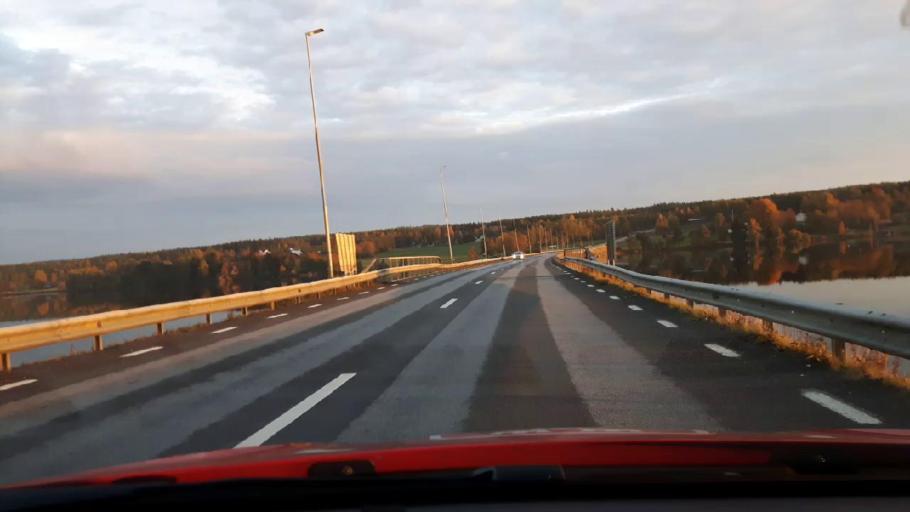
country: SE
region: Jaemtland
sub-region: OEstersunds Kommun
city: Lit
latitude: 63.3153
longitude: 14.8673
